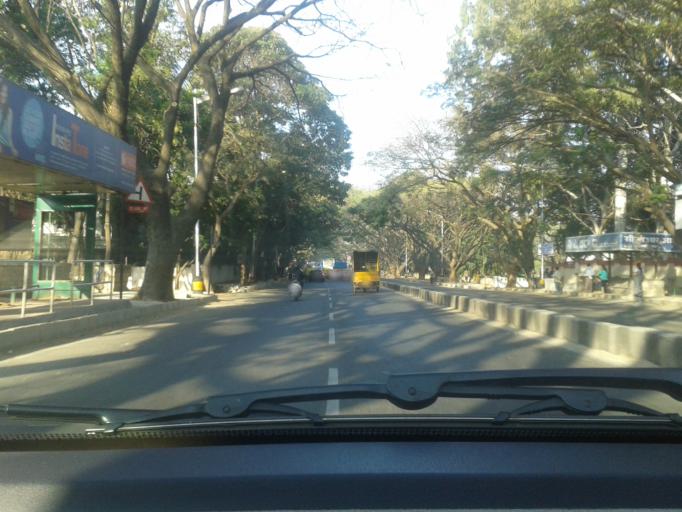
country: IN
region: Karnataka
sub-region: Bangalore Urban
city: Bangalore
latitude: 13.0148
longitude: 77.5751
